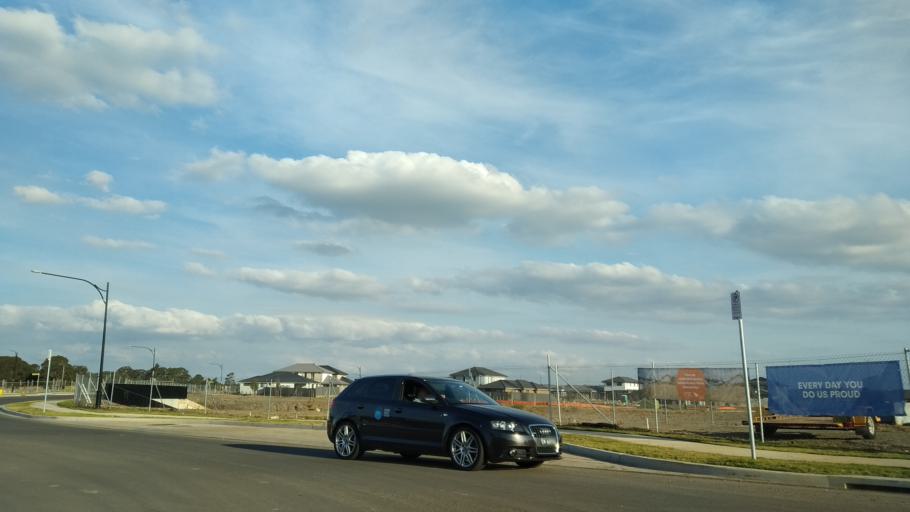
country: AU
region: New South Wales
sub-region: Penrith Municipality
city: Werrington County
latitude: -33.7296
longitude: 150.7549
